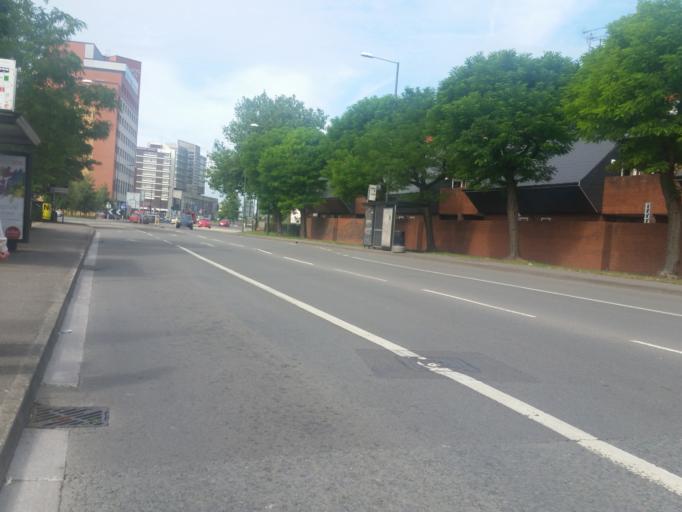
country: GB
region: England
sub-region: Borough of Swindon
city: Swindon
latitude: 51.5628
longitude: -1.7775
